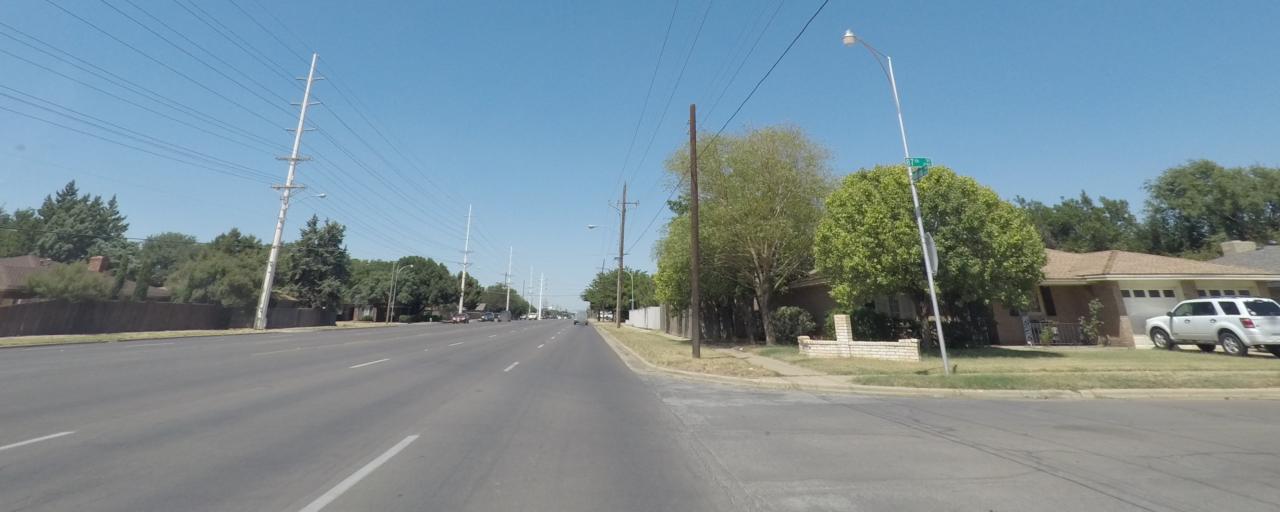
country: US
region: Texas
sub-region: Lubbock County
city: Lubbock
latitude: 33.5151
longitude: -101.8876
